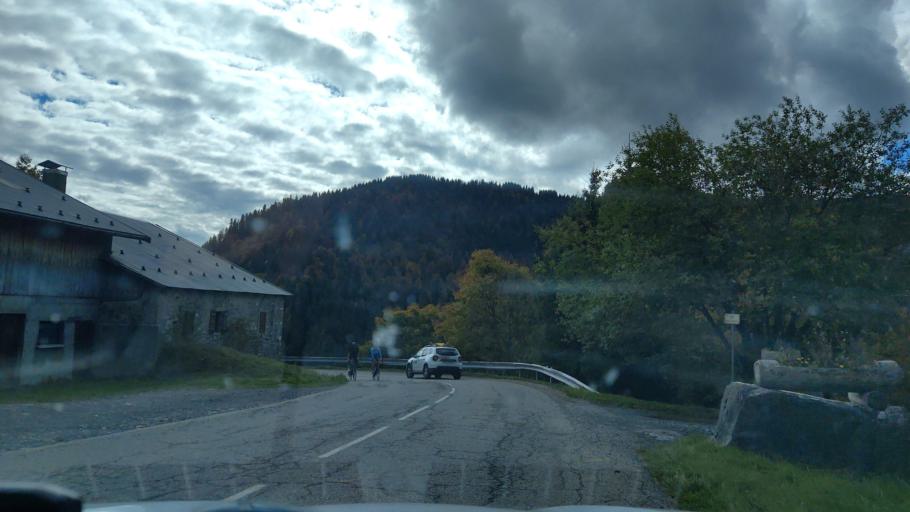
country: FR
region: Rhone-Alpes
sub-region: Departement de la Haute-Savoie
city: La Clusaz
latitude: 45.8688
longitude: 6.4834
